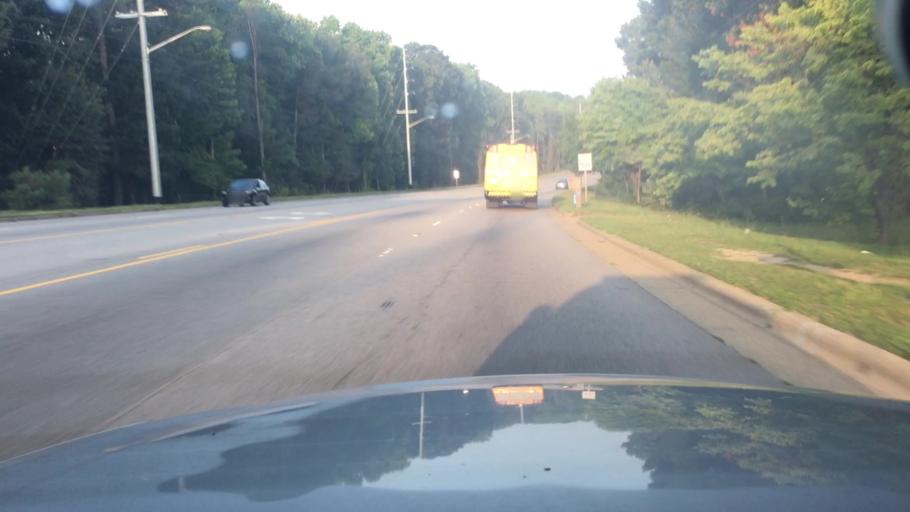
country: US
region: North Carolina
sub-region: Cumberland County
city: Fayetteville
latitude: 35.1014
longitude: -78.9025
